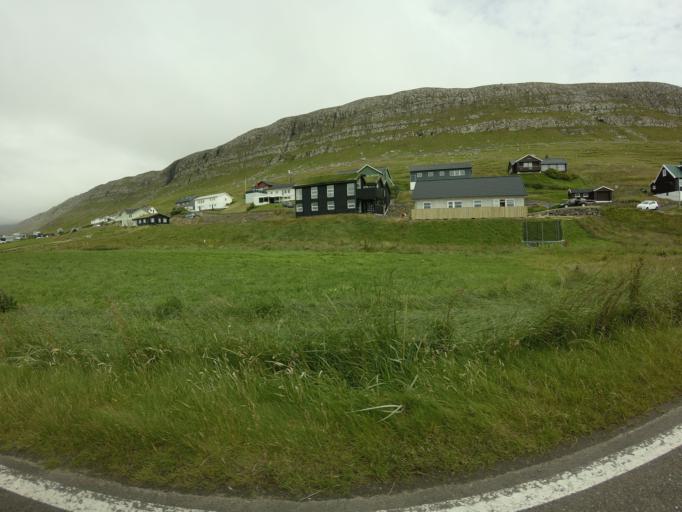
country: FO
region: Sandoy
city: Sandur
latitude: 61.8393
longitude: -6.8063
